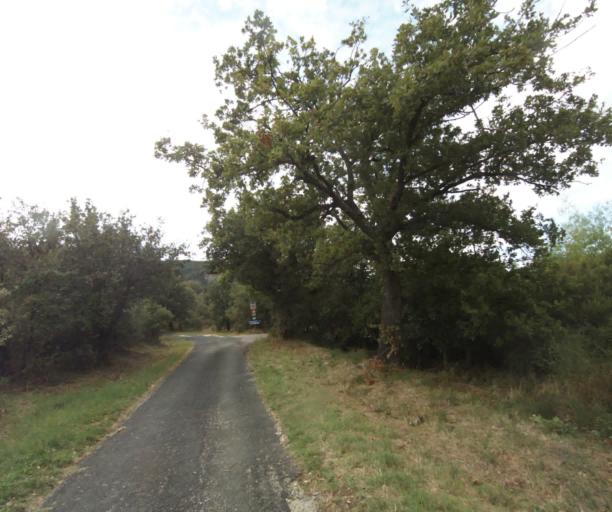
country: FR
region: Languedoc-Roussillon
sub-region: Departement des Pyrenees-Orientales
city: Argelers
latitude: 42.5307
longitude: 3.0101
